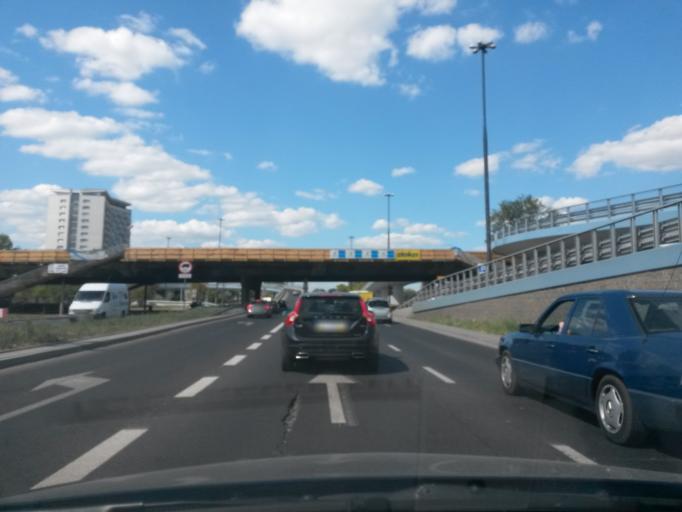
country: PL
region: Masovian Voivodeship
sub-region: Warszawa
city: Srodmiescie
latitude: 52.2236
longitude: 21.0442
